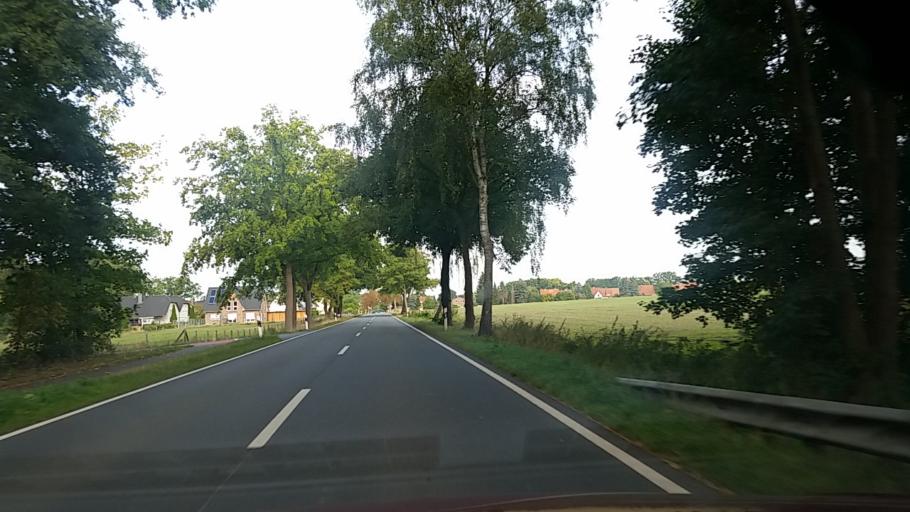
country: DE
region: Lower Saxony
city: Ahnsbeck
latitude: 52.6034
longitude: 10.2979
